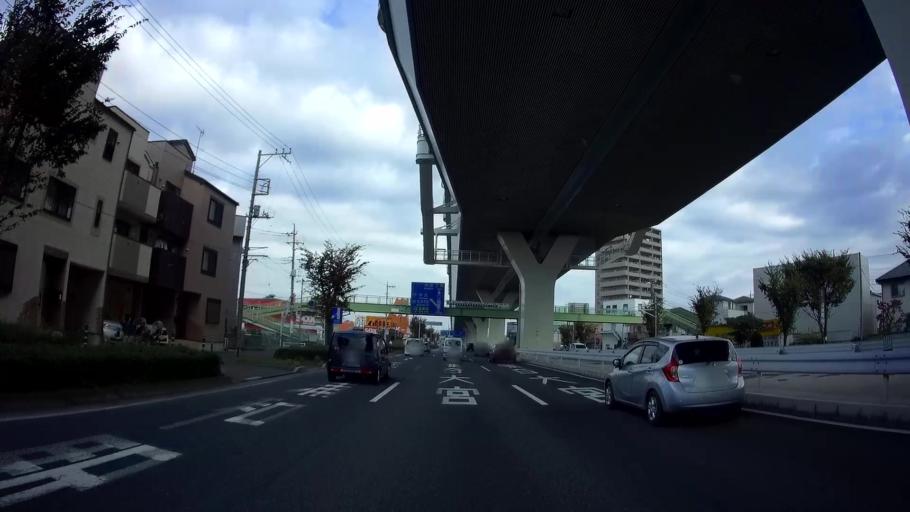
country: JP
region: Saitama
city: Yono
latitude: 35.8630
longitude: 139.6208
